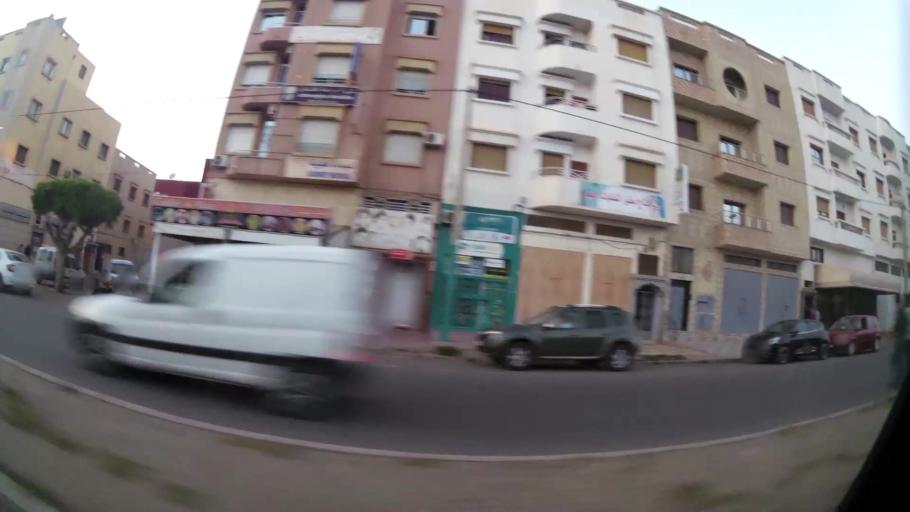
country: MA
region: Souss-Massa-Draa
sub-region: Inezgane-Ait Mellou
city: Inezgane
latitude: 30.3786
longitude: -9.5028
